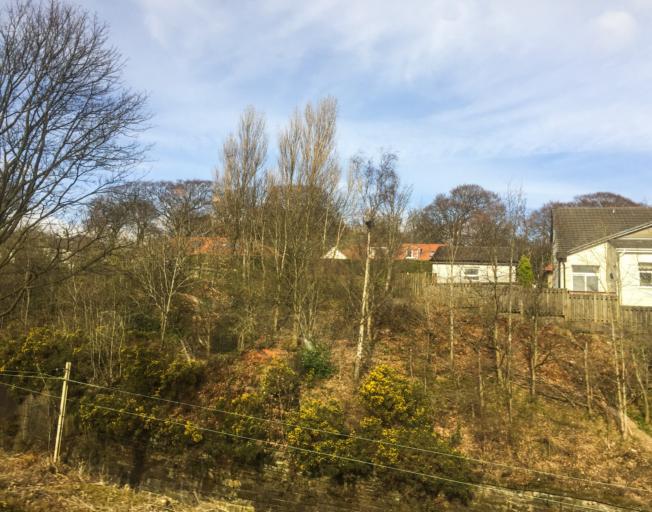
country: GB
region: Scotland
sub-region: East Dunbartonshire
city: Bearsden
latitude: 55.8991
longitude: -4.3235
